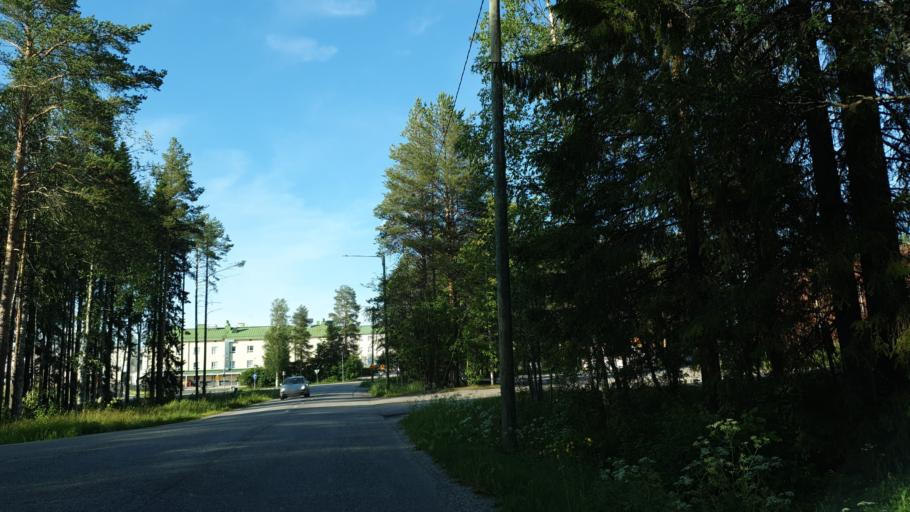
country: FI
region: Kainuu
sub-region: Kehys-Kainuu
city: Kuhmo
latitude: 64.1223
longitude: 29.5049
